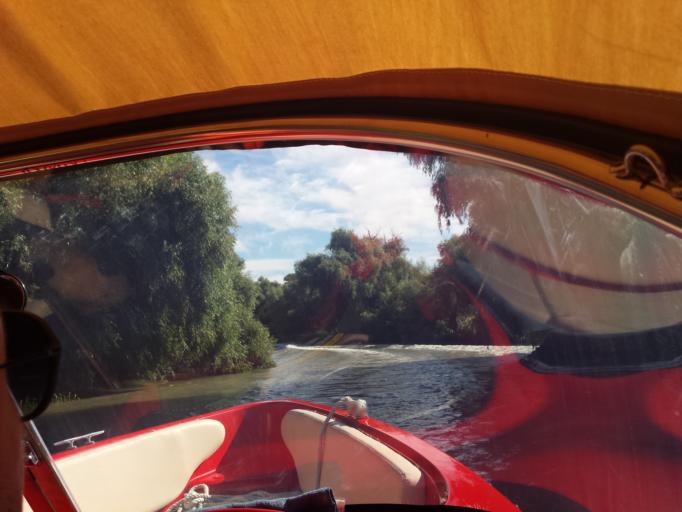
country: RO
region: Tulcea
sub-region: Comuna Pardina
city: Pardina
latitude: 45.2455
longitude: 29.0285
